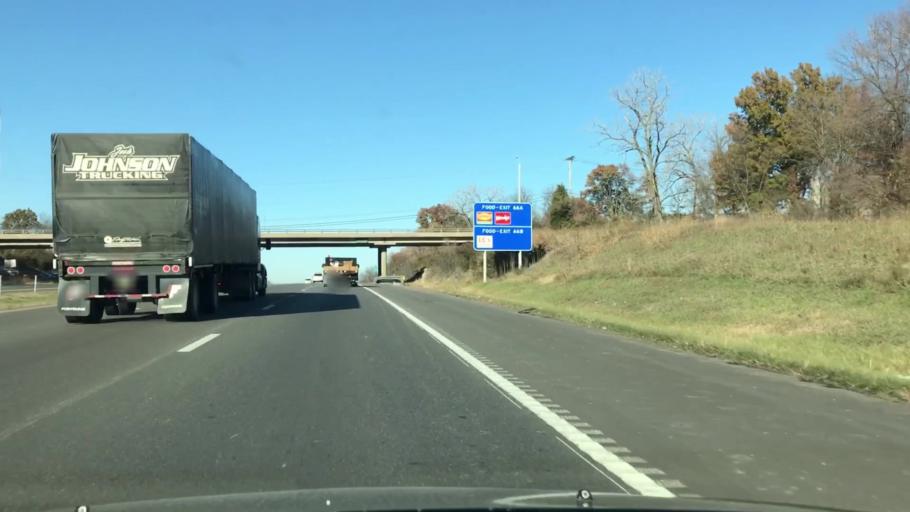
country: US
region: Missouri
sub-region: Jackson County
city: Raytown
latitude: 39.0020
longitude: -94.5017
